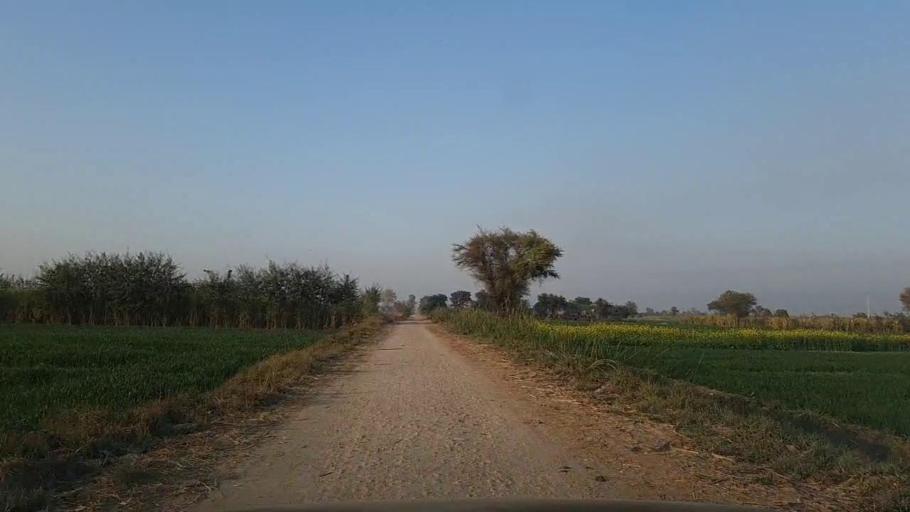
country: PK
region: Sindh
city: Daur
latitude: 26.4823
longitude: 68.4179
